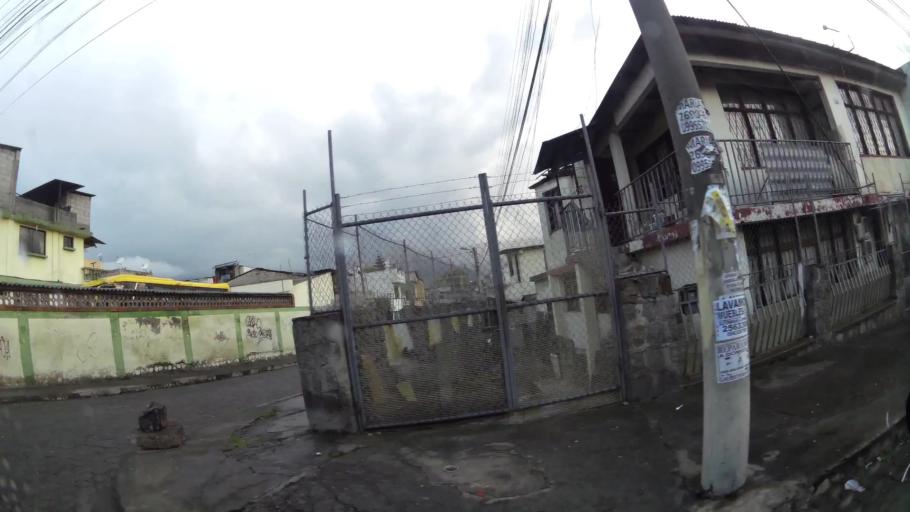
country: EC
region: Pichincha
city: Quito
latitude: -0.2964
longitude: -78.5390
